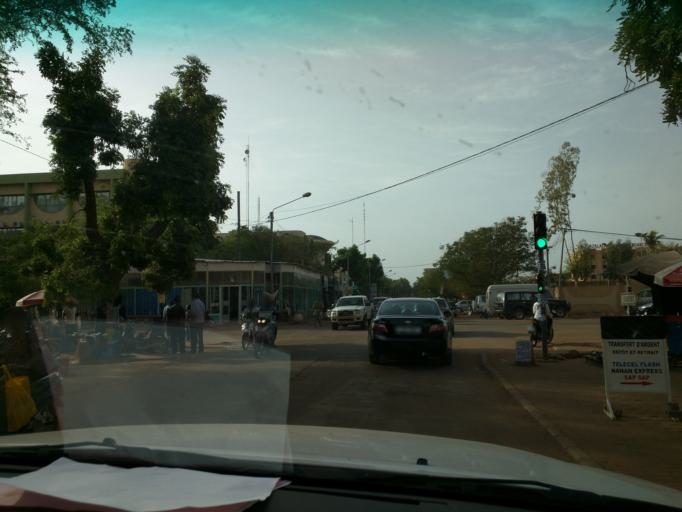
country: BF
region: Centre
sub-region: Kadiogo Province
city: Ouagadougou
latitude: 12.3695
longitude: -1.5156
